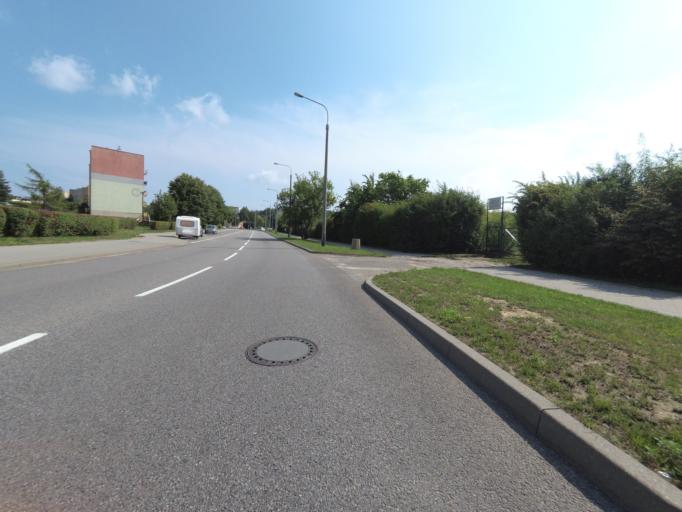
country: PL
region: Pomeranian Voivodeship
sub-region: Gdynia
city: Wielki Kack
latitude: 54.4932
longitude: 18.5078
